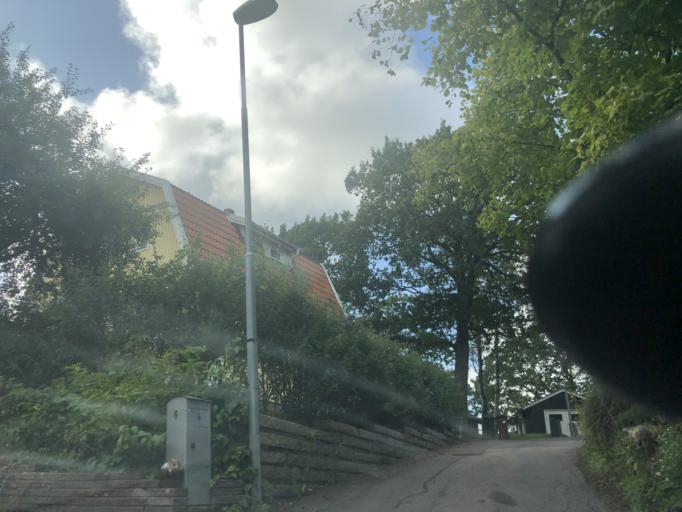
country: SE
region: Vaestra Goetaland
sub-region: Goteborg
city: Goeteborg
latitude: 57.7458
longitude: 11.9546
